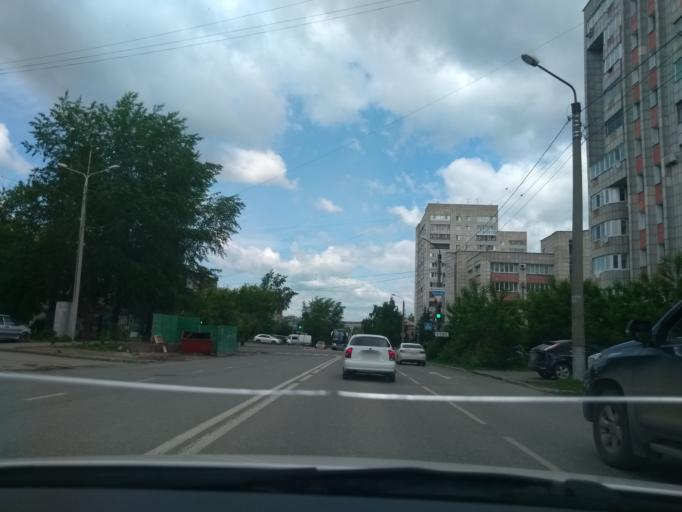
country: RU
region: Perm
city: Perm
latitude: 58.0023
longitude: 56.2157
